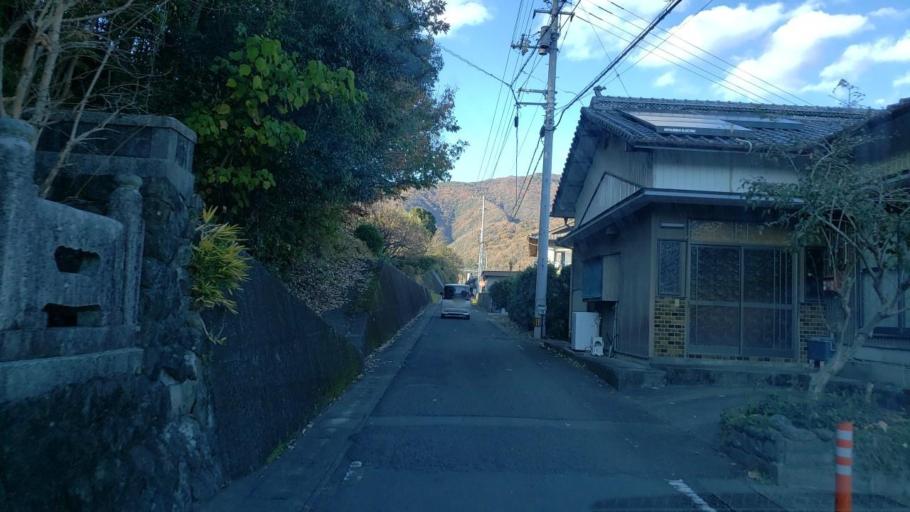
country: JP
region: Tokushima
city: Wakimachi
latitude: 34.0645
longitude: 134.0877
